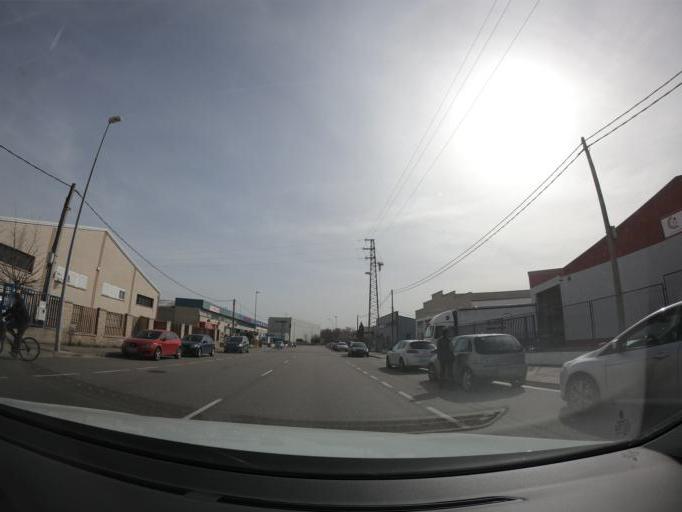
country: ES
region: Basque Country
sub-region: Provincia de Alava
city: Oyon
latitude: 42.4755
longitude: -2.4033
